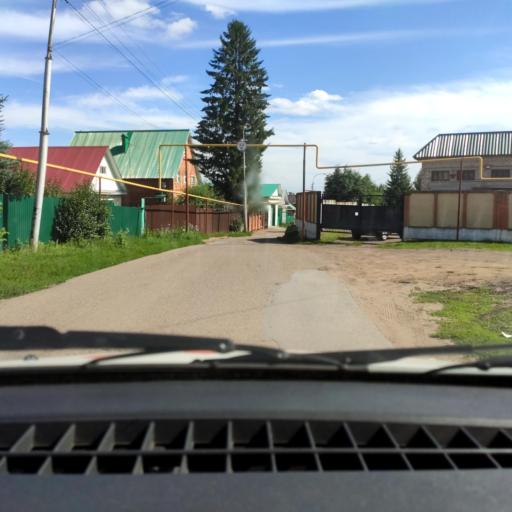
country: RU
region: Bashkortostan
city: Blagoveshchensk
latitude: 55.0473
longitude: 55.9605
